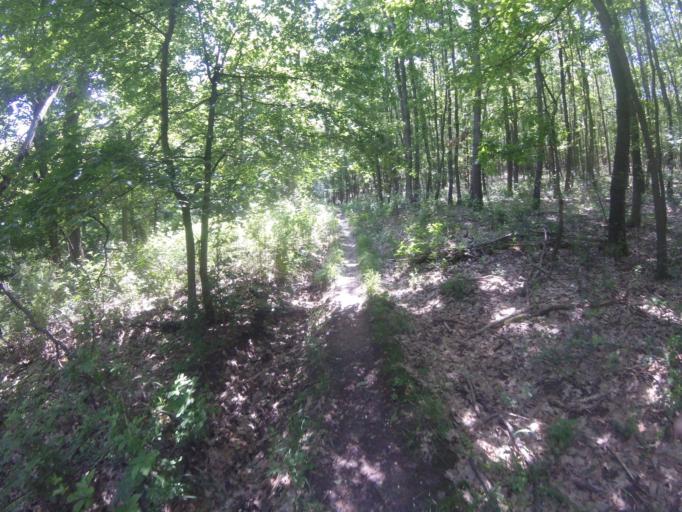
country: HU
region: Nograd
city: Matraverebely
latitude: 47.9317
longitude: 19.7963
